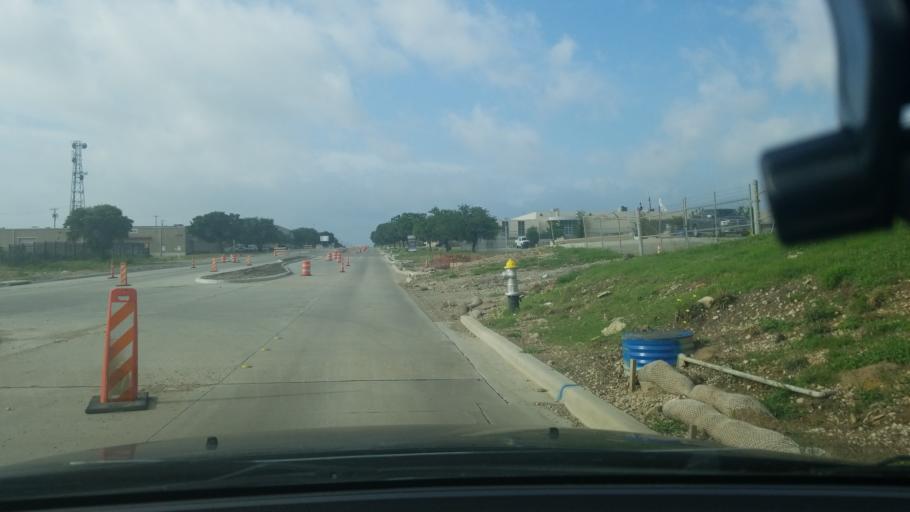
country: US
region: Texas
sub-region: Dallas County
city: Mesquite
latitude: 32.7762
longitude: -96.6467
